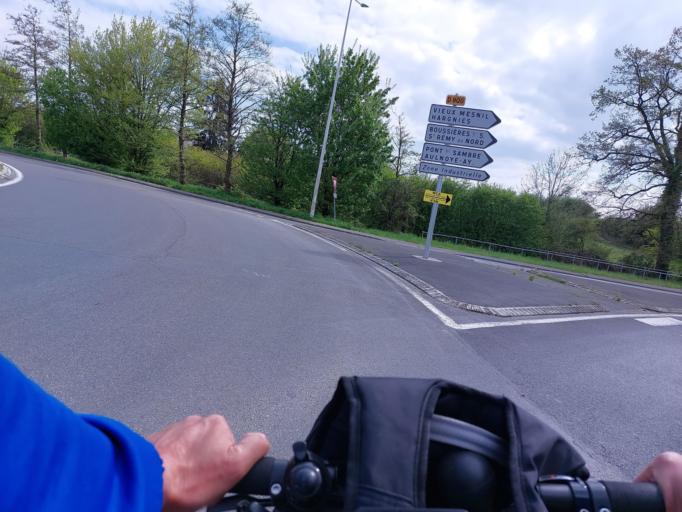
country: FR
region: Nord-Pas-de-Calais
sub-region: Departement du Nord
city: Hautmont
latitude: 50.2647
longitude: 3.8984
